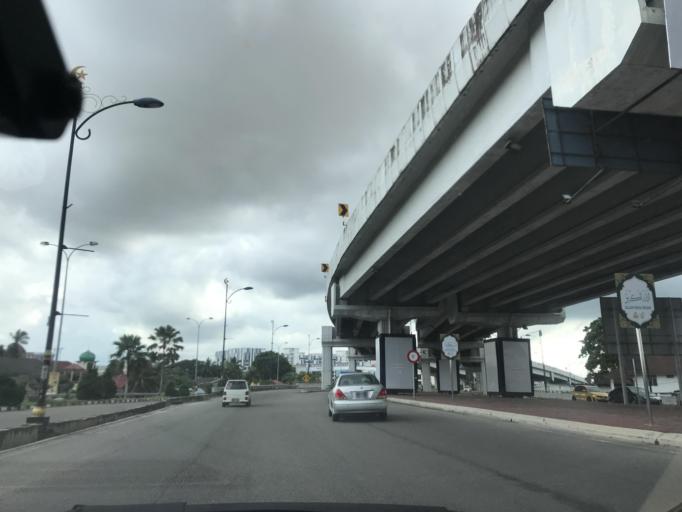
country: MY
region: Kelantan
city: Kota Bharu
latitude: 6.1157
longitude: 102.2359
